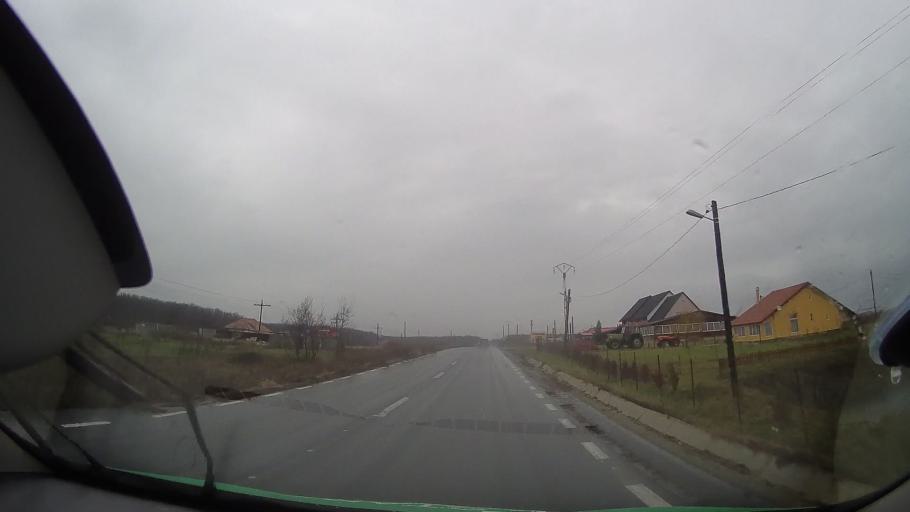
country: RO
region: Bihor
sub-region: Comuna Olcea
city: Olcea
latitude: 46.6877
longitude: 21.9659
